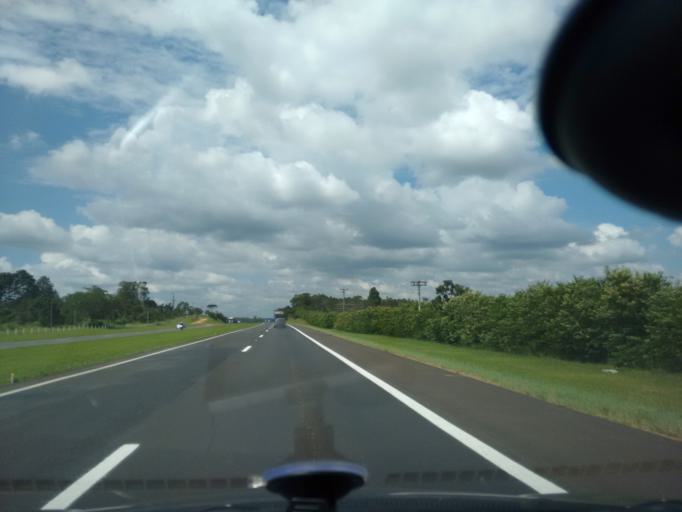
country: BR
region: Sao Paulo
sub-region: Sao Carlos
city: Sao Carlos
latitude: -22.0795
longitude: -47.8400
